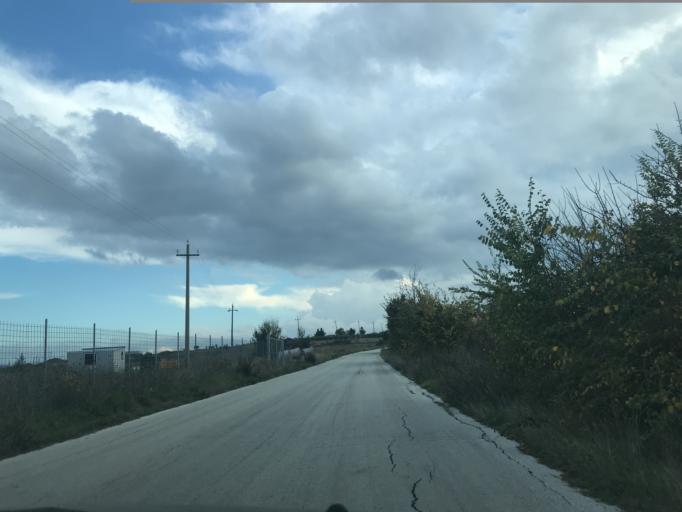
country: IT
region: Molise
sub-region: Provincia di Isernia
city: Bagnoli del Trigno
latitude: 41.6939
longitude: 14.4619
